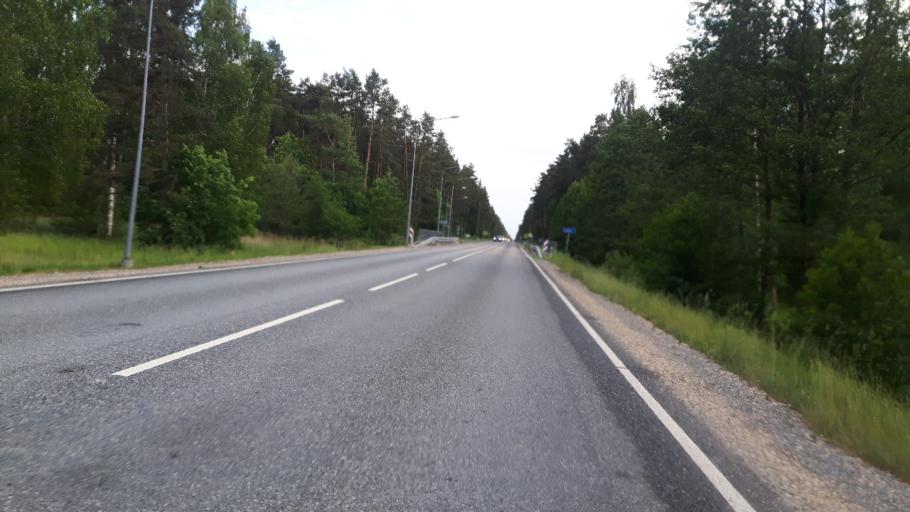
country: LV
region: Riga
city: Jaunciems
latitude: 57.0798
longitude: 24.1593
